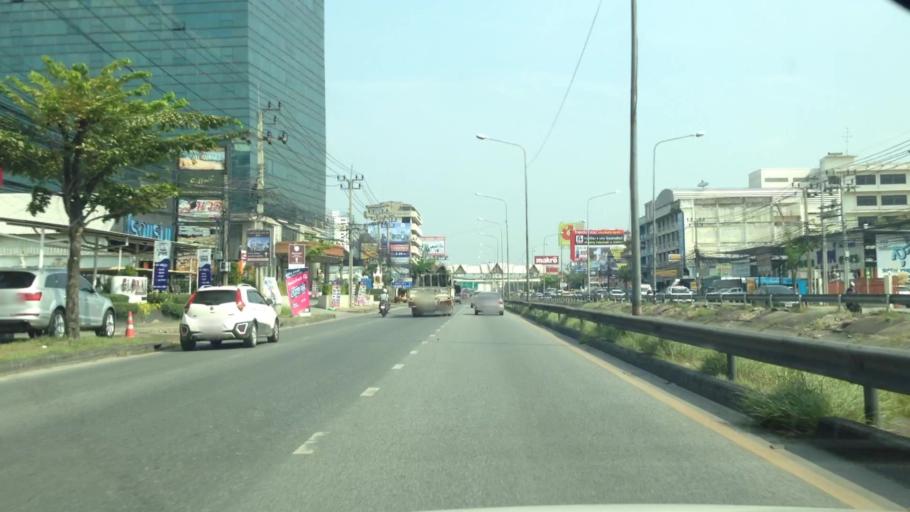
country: TH
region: Bangkok
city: Bang Na
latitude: 13.6469
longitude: 100.6382
